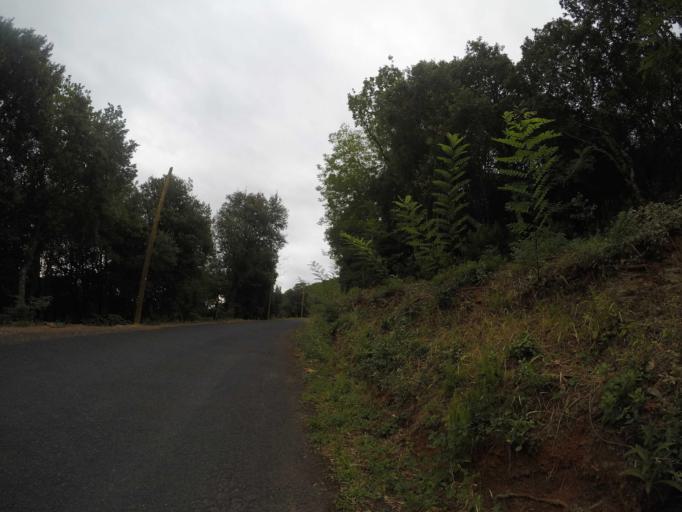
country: FR
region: Languedoc-Roussillon
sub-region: Departement des Pyrenees-Orientales
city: Ille-sur-Tet
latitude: 42.6293
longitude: 2.6121
